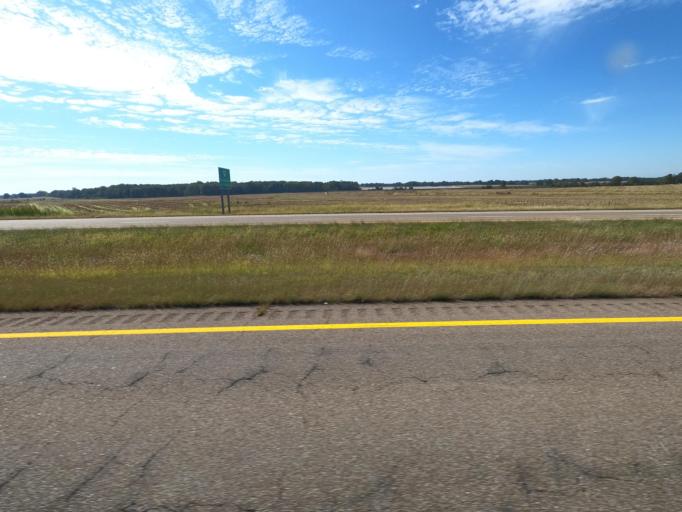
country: US
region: Tennessee
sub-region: Crockett County
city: Alamo
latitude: 35.8278
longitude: -89.1763
